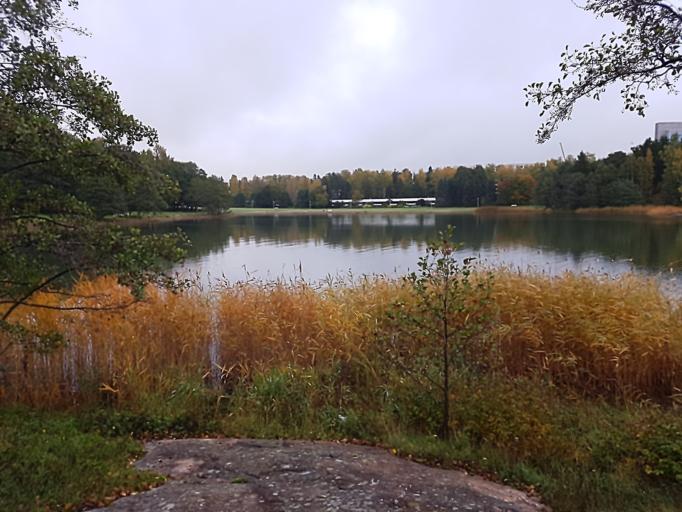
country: FI
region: Uusimaa
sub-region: Helsinki
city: Otaniemi
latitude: 60.1749
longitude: 24.8182
